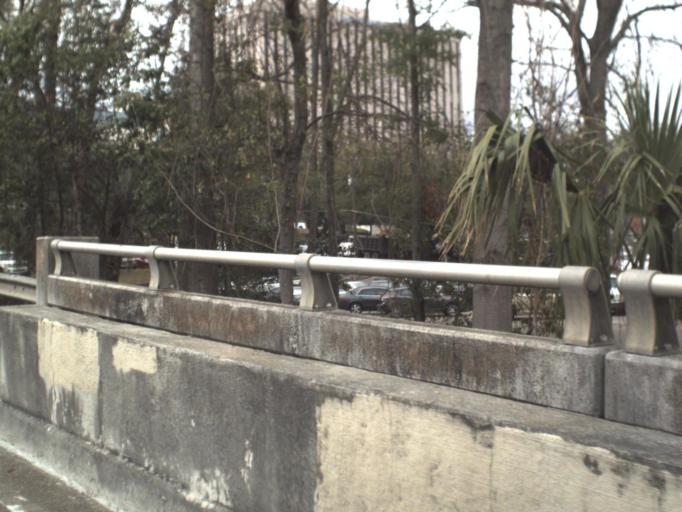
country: US
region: Florida
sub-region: Leon County
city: Tallahassee
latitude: 30.4382
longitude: -84.2771
